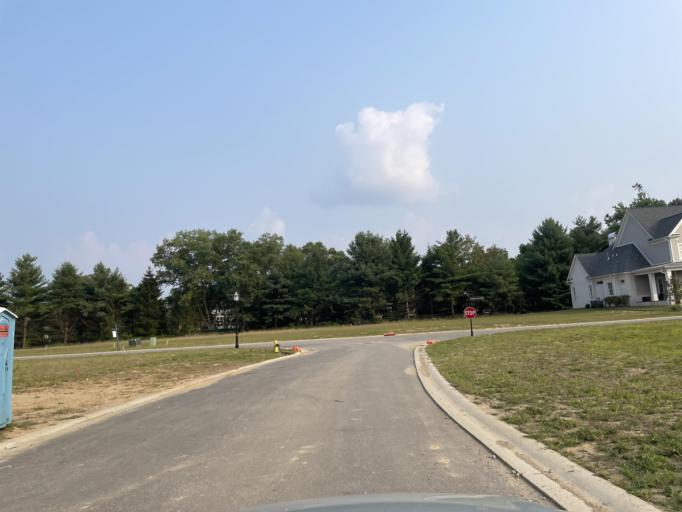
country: US
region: Kentucky
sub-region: Jefferson County
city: Prospect
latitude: 38.3570
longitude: -85.6224
